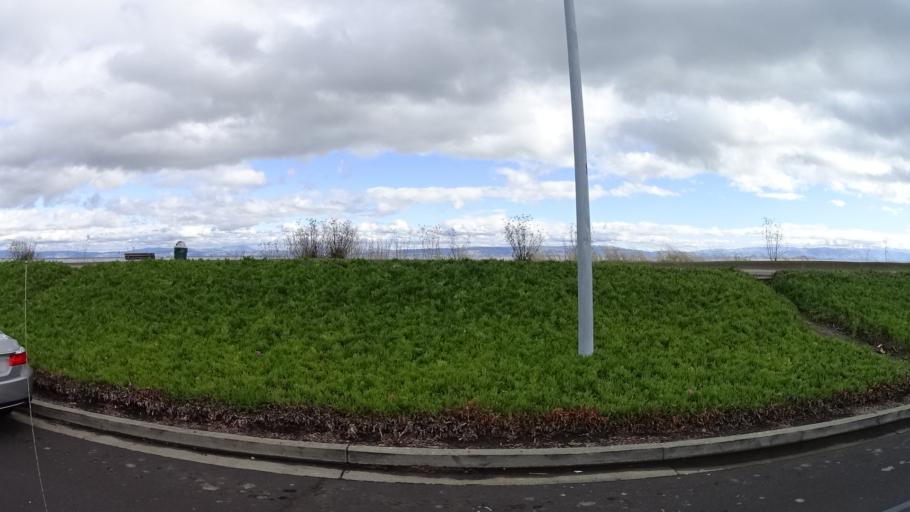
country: US
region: California
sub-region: San Mateo County
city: Foster City
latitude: 37.5626
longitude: -122.2491
